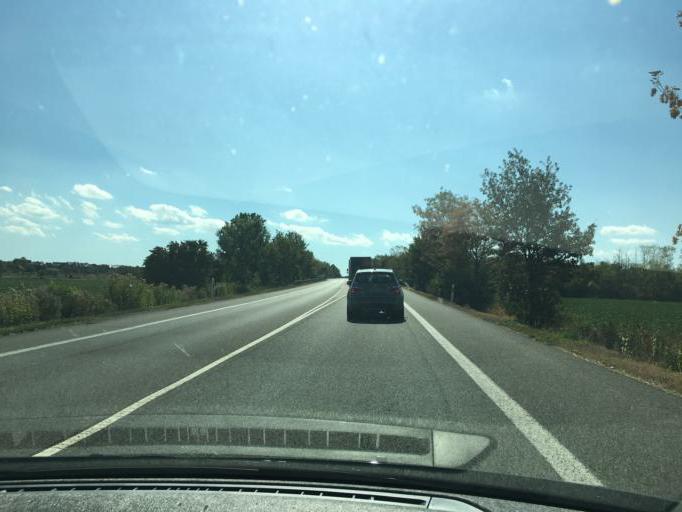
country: DE
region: North Rhine-Westphalia
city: Zulpich
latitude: 50.6924
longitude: 6.6360
